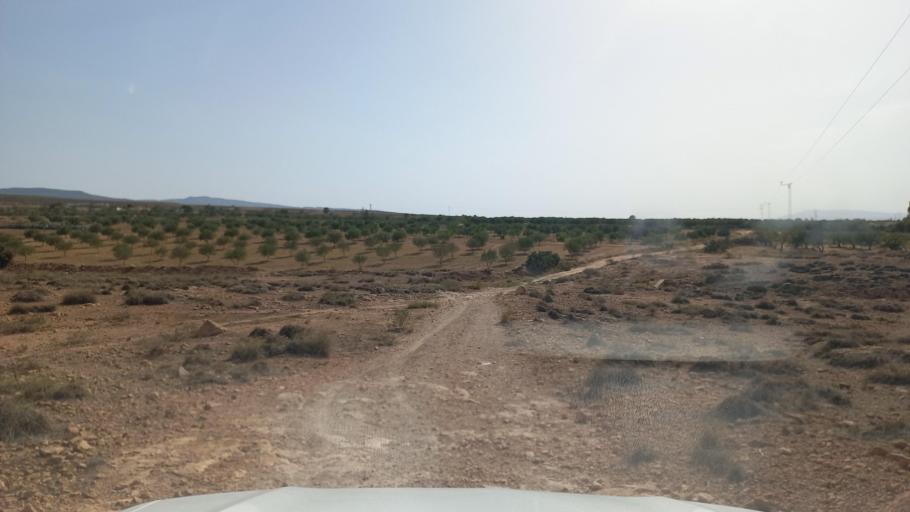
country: TN
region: Al Qasrayn
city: Kasserine
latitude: 35.2064
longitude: 8.9727
